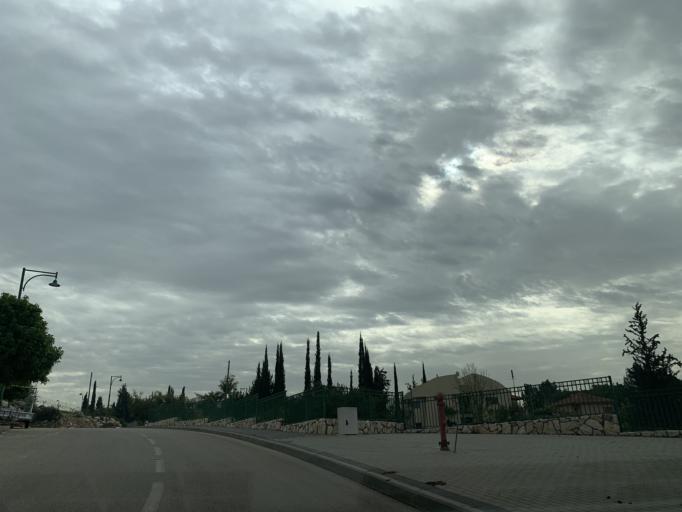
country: IL
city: Nirit
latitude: 32.1485
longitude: 34.9871
